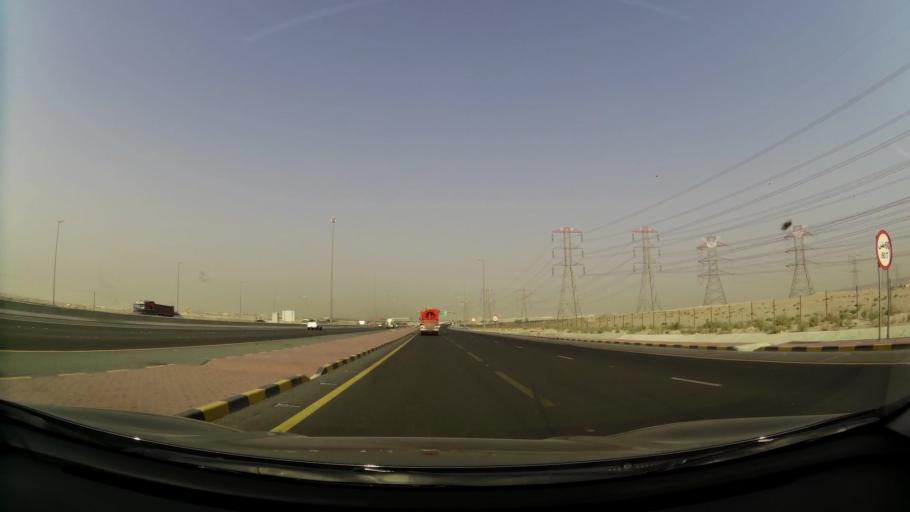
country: KW
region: Al Asimah
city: Ar Rabiyah
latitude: 29.2490
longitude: 47.8703
